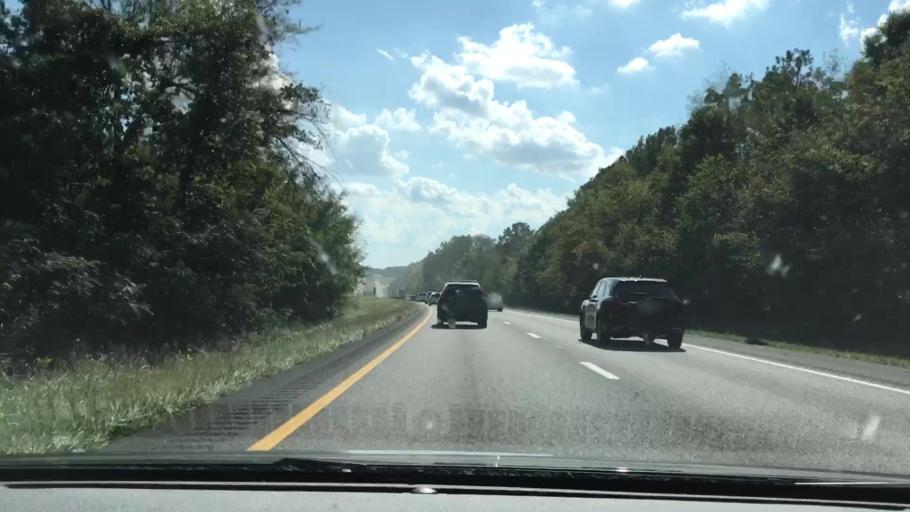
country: US
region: Tennessee
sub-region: Robertson County
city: Cross Plains
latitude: 36.5426
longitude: -86.6371
